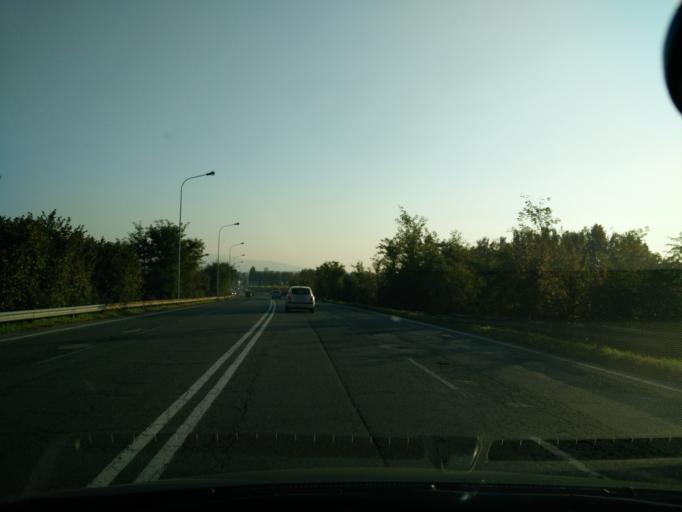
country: IT
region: Piedmont
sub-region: Provincia di Torino
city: Borgaro Torinese
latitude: 45.1305
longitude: 7.7034
